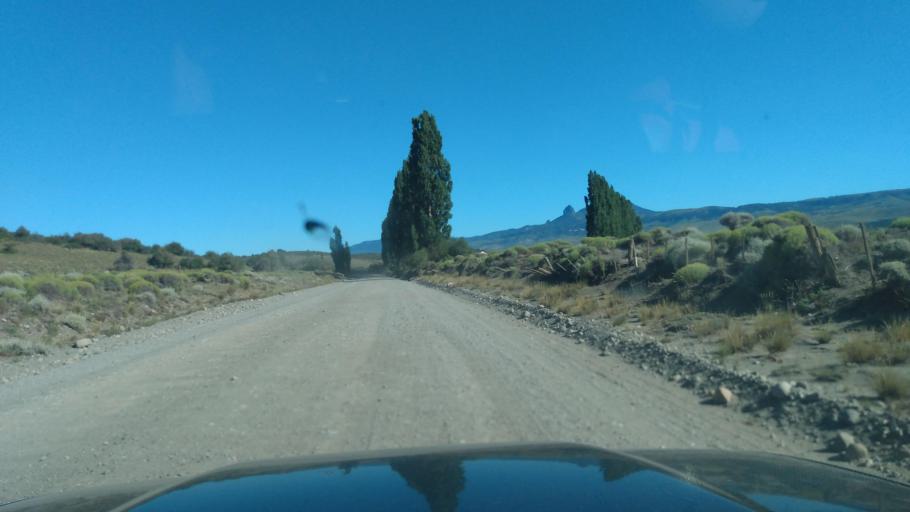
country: AR
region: Neuquen
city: Junin de los Andes
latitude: -39.8317
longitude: -71.1913
